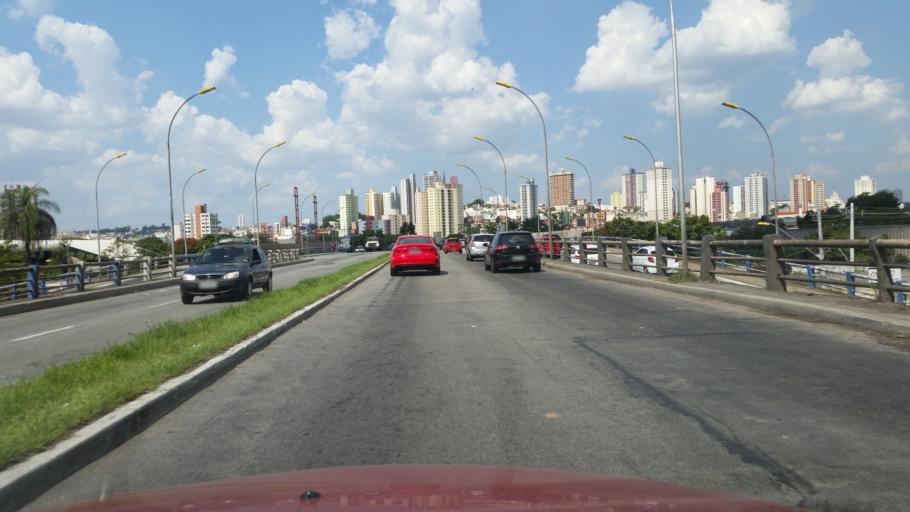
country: BR
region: Sao Paulo
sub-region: Sao Caetano Do Sul
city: Sao Caetano do Sul
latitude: -23.6394
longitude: -46.5374
